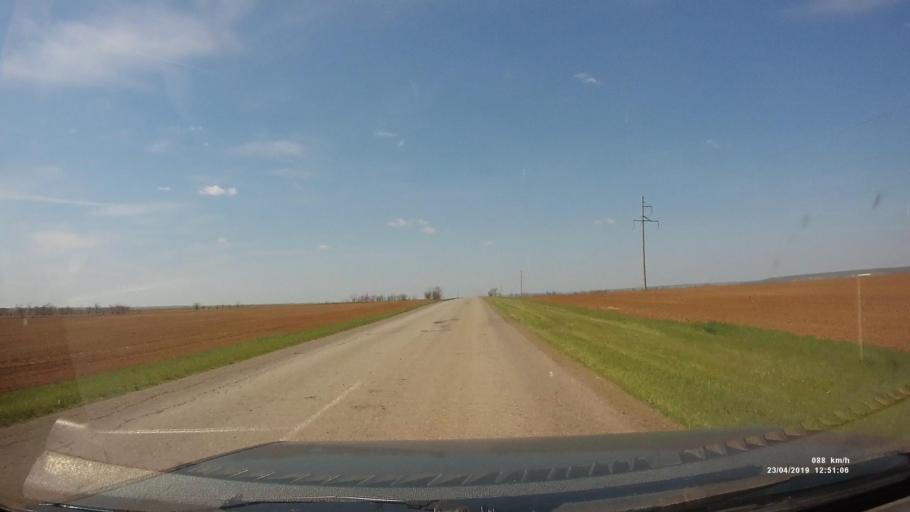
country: RU
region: Kalmykiya
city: Yashalta
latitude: 46.5516
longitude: 42.6272
